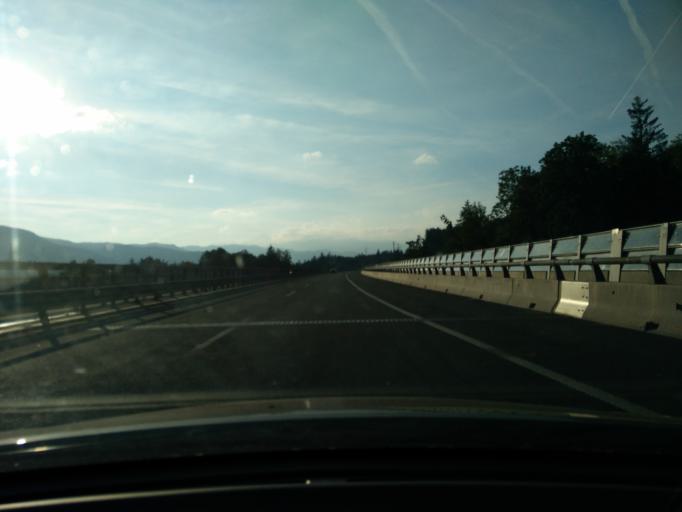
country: SI
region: Radovljica
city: Radovljica
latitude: 46.3278
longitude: 14.2144
